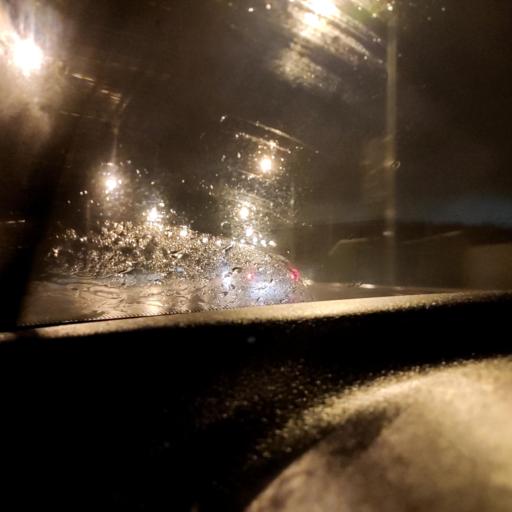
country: RU
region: Samara
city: Petra-Dubrava
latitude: 53.3063
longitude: 50.2387
